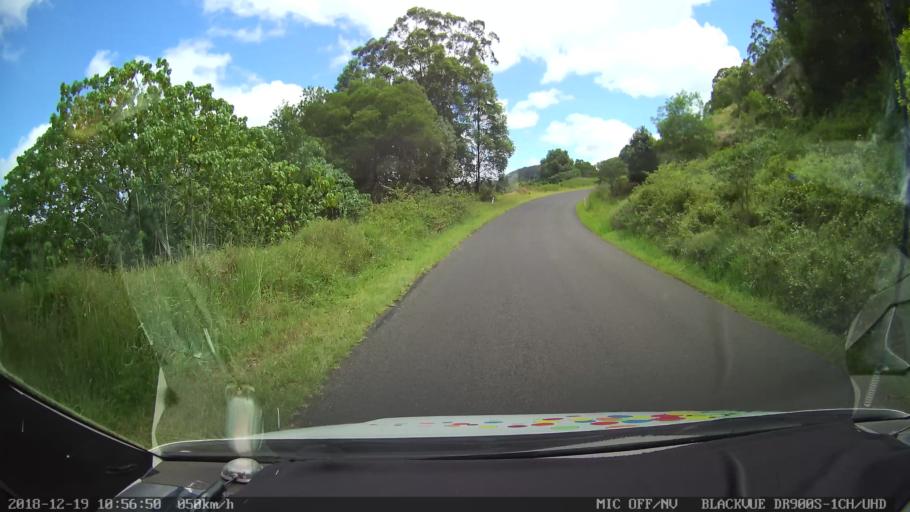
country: AU
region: New South Wales
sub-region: Lismore Municipality
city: Nimbin
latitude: -28.5917
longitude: 153.2609
